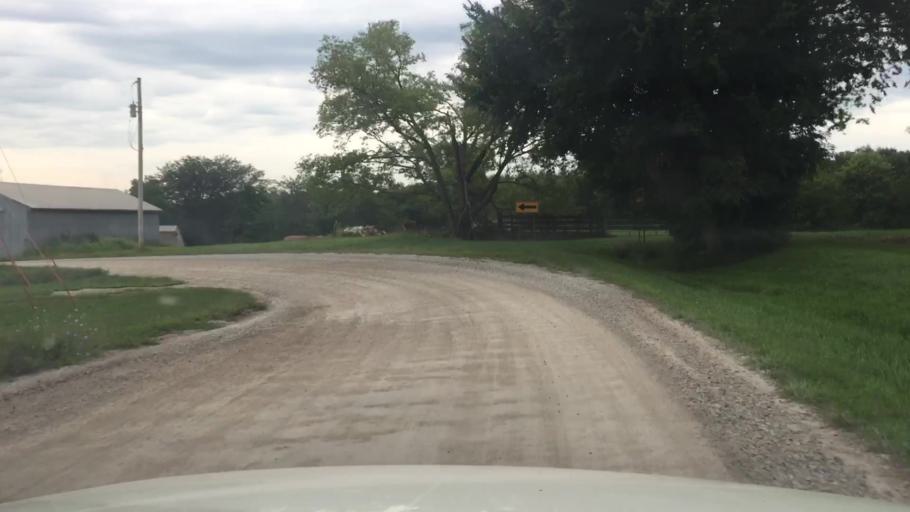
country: US
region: Iowa
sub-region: Story County
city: Huxley
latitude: 41.9118
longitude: -93.5766
